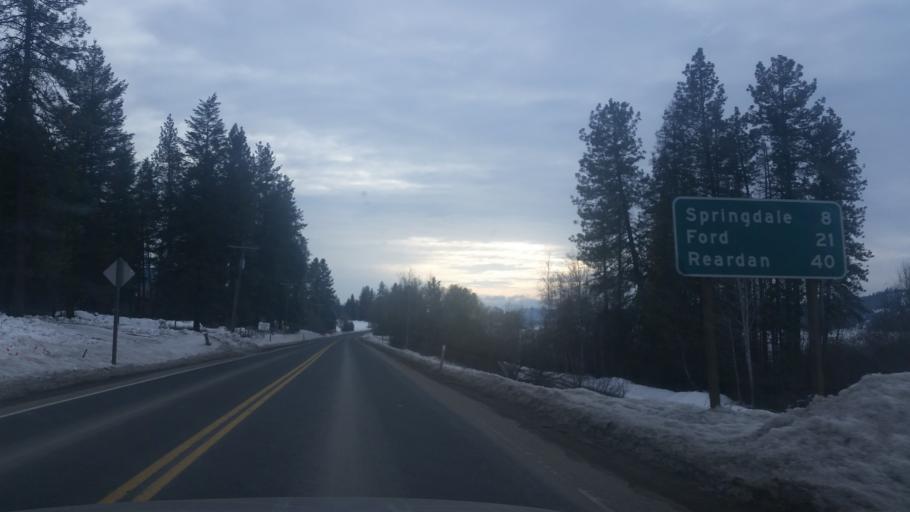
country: US
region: Washington
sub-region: Stevens County
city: Chewelah
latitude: 48.1651
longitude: -117.7232
